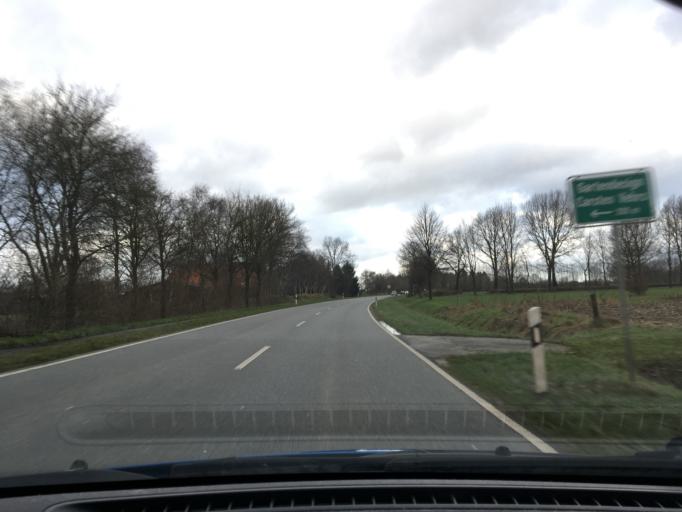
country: DE
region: Schleswig-Holstein
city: Kaisborstel
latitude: 54.0186
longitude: 9.4777
